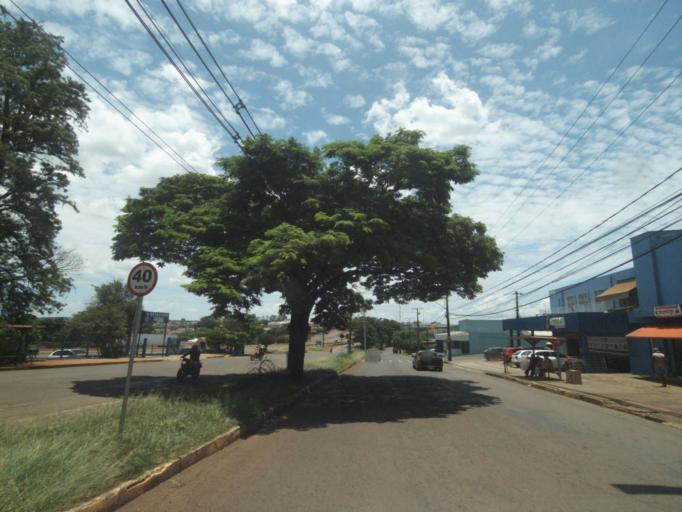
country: BR
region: Parana
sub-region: Londrina
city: Londrina
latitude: -23.3724
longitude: -51.1380
